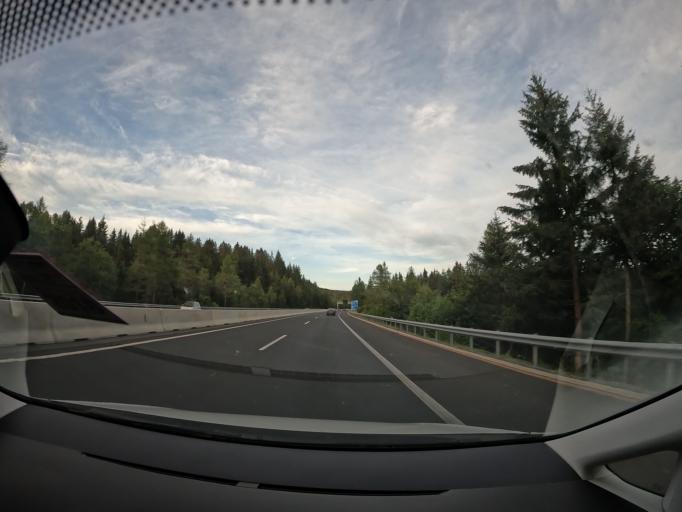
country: AT
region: Carinthia
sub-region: Politischer Bezirk Wolfsberg
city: Preitenegg
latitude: 46.9665
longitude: 14.9309
